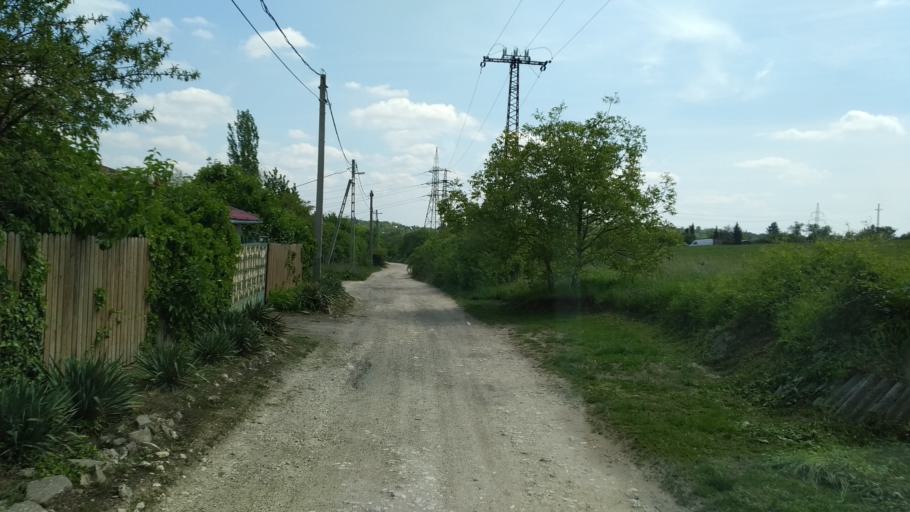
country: HU
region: Pest
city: Urom
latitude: 47.6177
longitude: 19.0257
